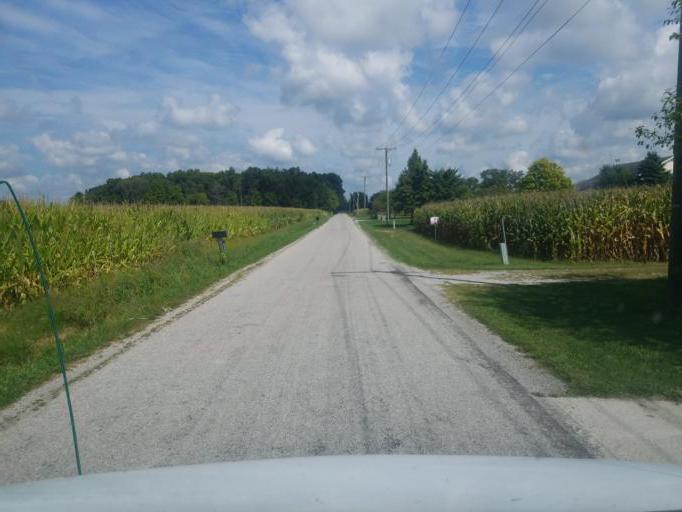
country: US
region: Ohio
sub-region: Marion County
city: Marion
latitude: 40.5144
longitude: -83.0838
